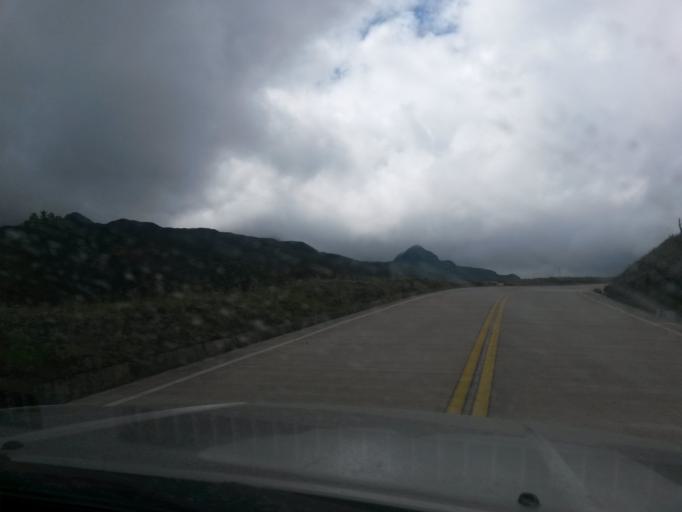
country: CO
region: Cauca
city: Totoro
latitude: 2.4968
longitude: -76.2365
